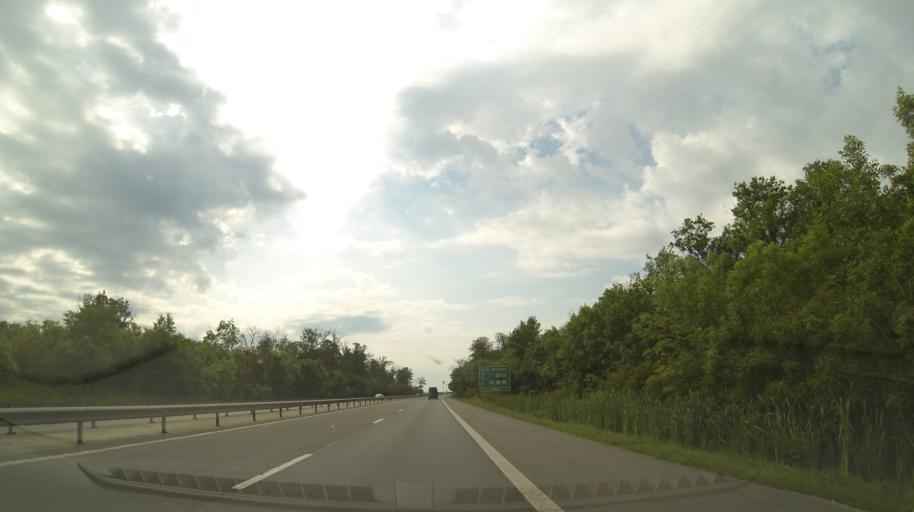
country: RO
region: Dambovita
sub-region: Comuna Uliesti
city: Uliesti
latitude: 44.6125
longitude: 25.4488
